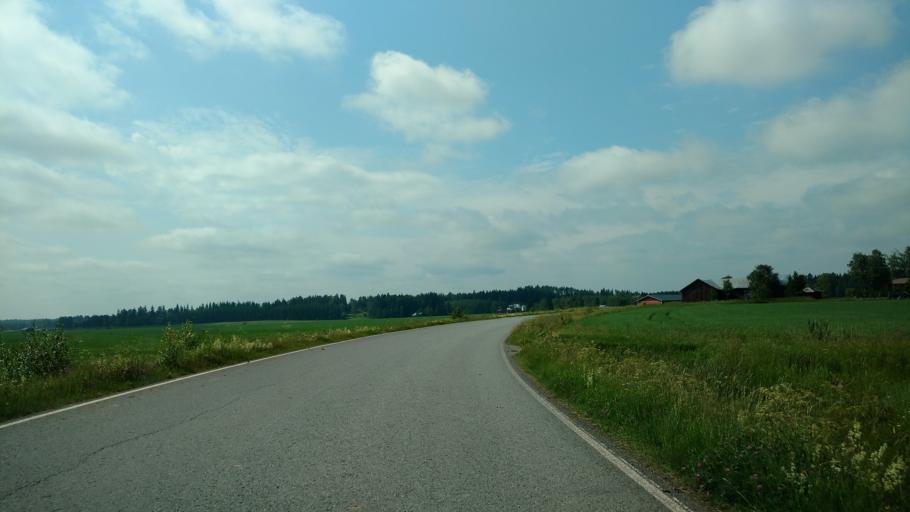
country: FI
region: Haeme
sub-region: Forssa
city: Ypaejae
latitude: 60.7886
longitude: 23.3795
